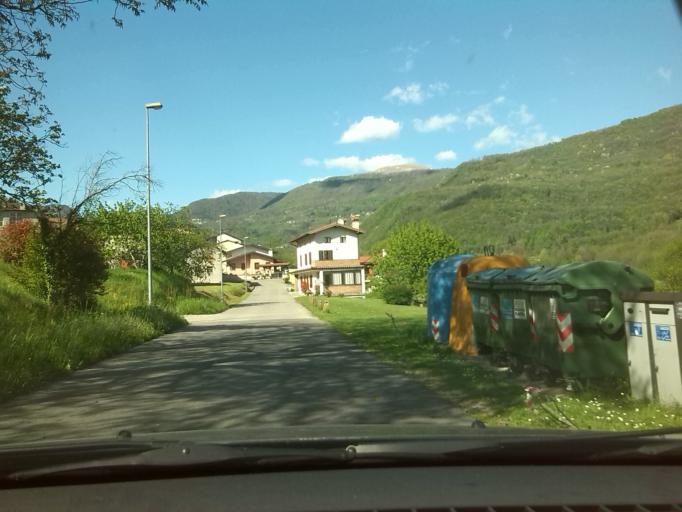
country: IT
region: Friuli Venezia Giulia
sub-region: Provincia di Udine
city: Pulfero
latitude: 46.1470
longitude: 13.4826
